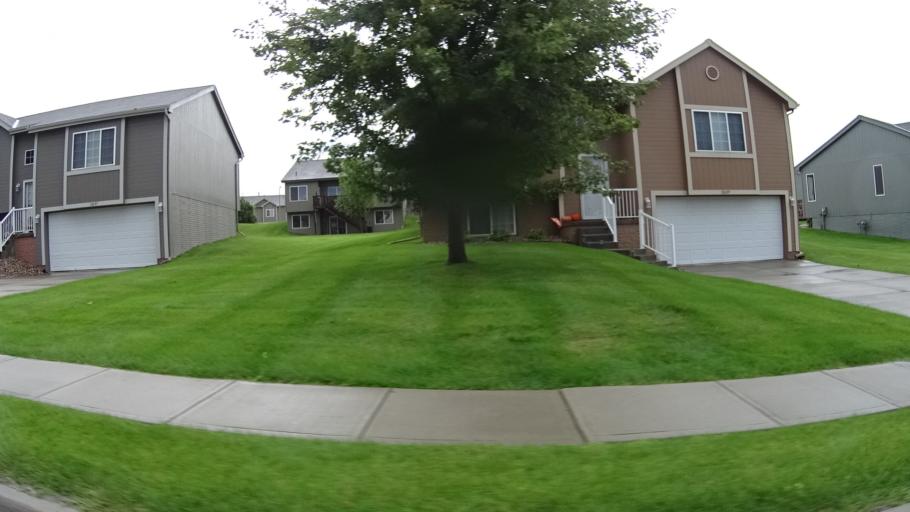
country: US
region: Nebraska
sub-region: Sarpy County
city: Offutt Air Force Base
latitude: 41.1550
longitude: -95.9496
